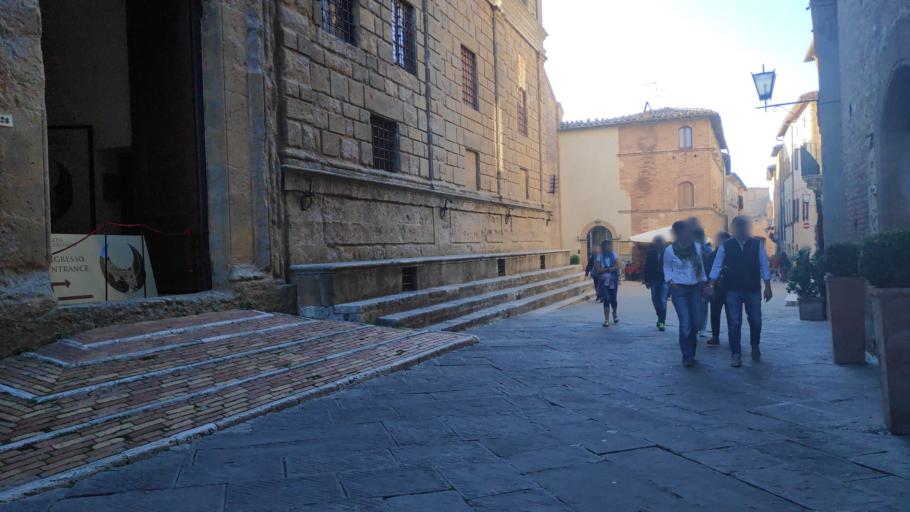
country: IT
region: Tuscany
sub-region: Provincia di Siena
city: Pienza
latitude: 43.0767
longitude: 11.6787
